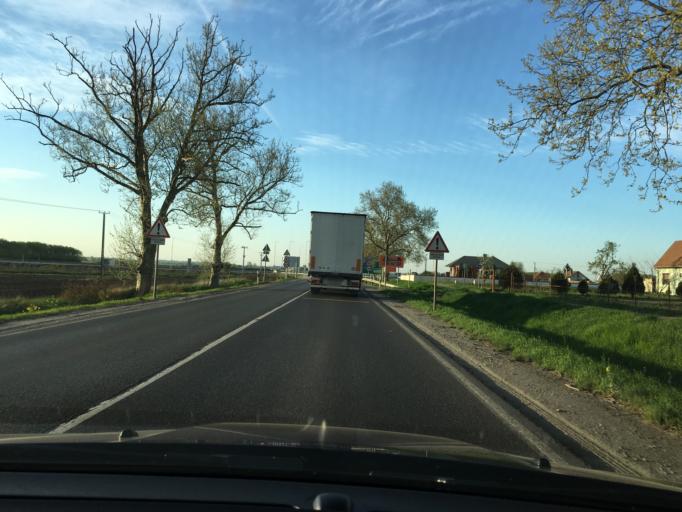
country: HU
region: Hajdu-Bihar
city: Mikepercs
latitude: 47.4604
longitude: 21.6366
